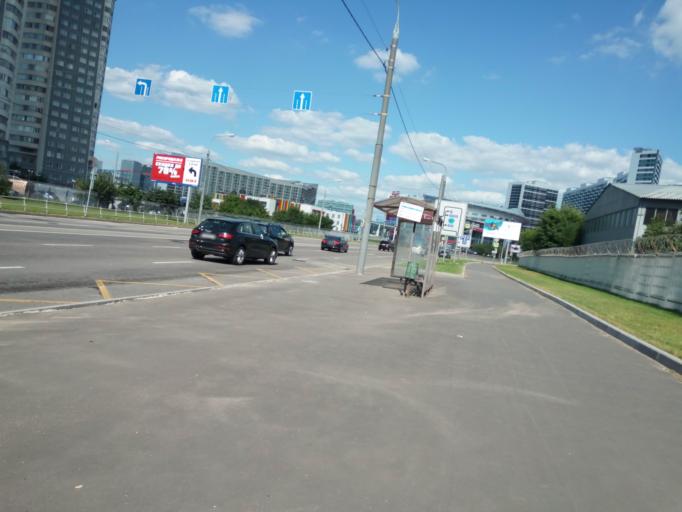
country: RU
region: Moscow
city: Sokol
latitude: 55.7829
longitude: 37.5347
